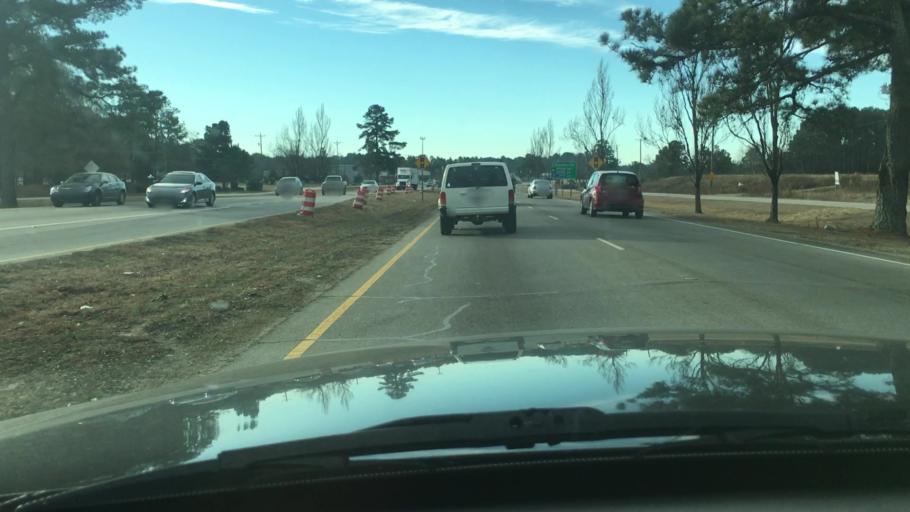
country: US
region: North Carolina
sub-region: Cumberland County
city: Fayetteville
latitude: 35.0033
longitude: -78.8993
